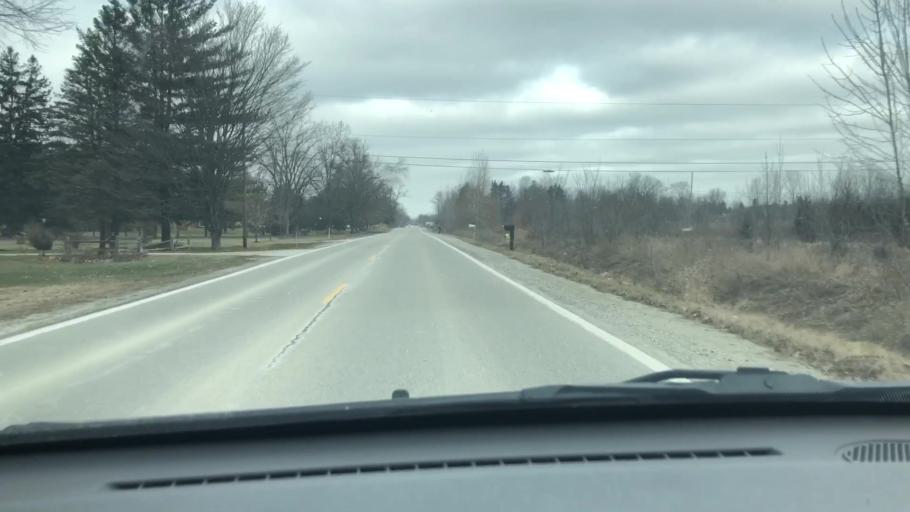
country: US
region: Michigan
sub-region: Macomb County
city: Shelby
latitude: 42.7354
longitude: -83.0172
